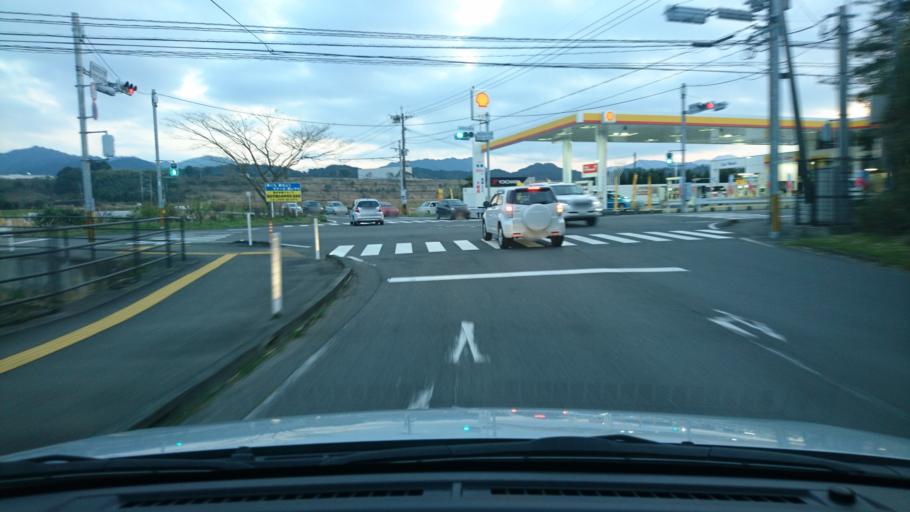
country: JP
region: Miyazaki
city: Miyazaki-shi
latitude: 31.8433
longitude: 131.4073
